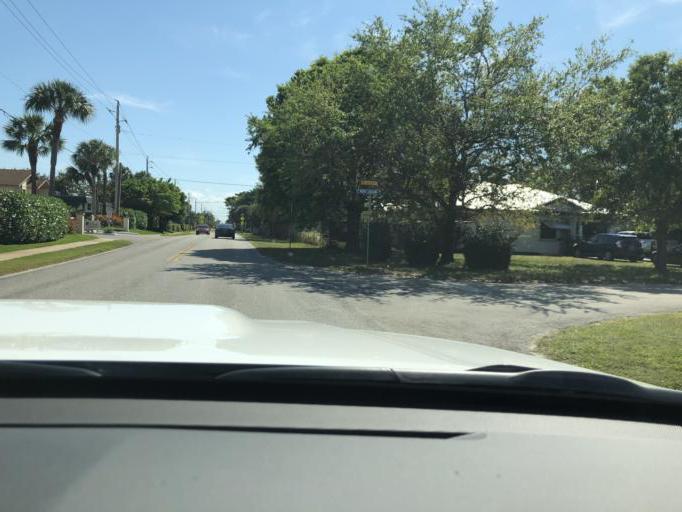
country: US
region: Florida
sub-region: Martin County
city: Stuart
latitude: 27.1831
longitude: -80.2571
